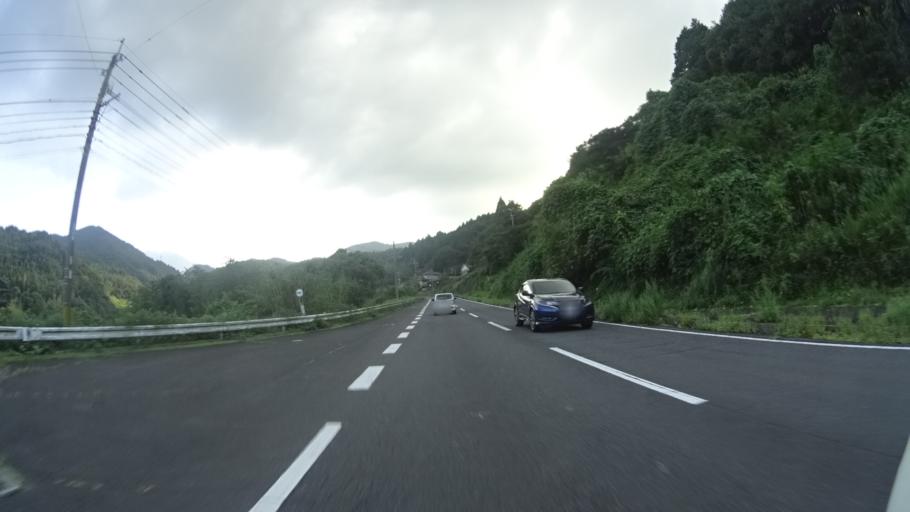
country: JP
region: Oita
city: Beppu
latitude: 33.3435
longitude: 131.4007
